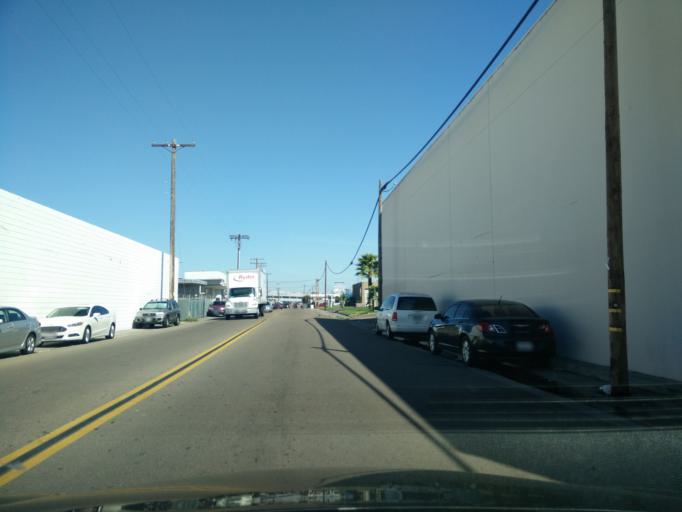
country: US
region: California
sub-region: San Diego County
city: San Diego
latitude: 32.7518
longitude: -117.2032
